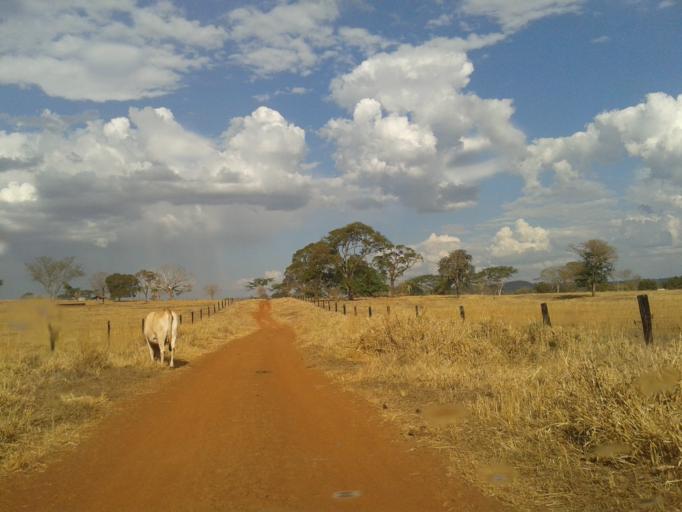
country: BR
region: Minas Gerais
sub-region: Santa Vitoria
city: Santa Vitoria
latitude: -19.1695
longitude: -49.9971
